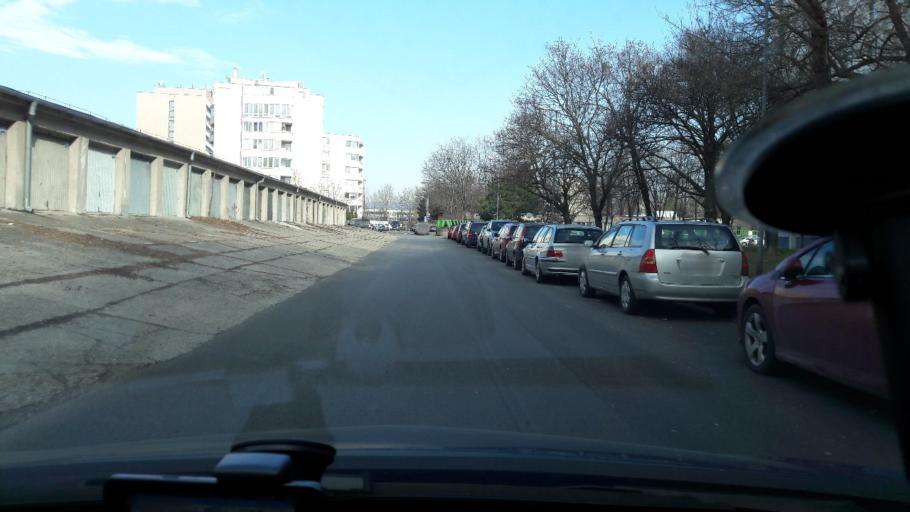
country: SK
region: Bratislavsky
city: Bratislava
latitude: 48.1511
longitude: 17.1510
